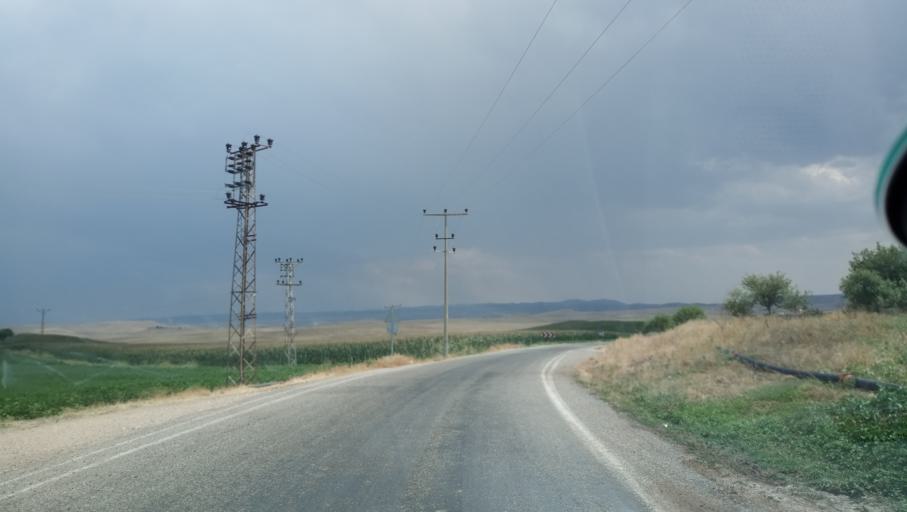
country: TR
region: Mardin
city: Baskavak
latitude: 37.6786
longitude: 40.8494
